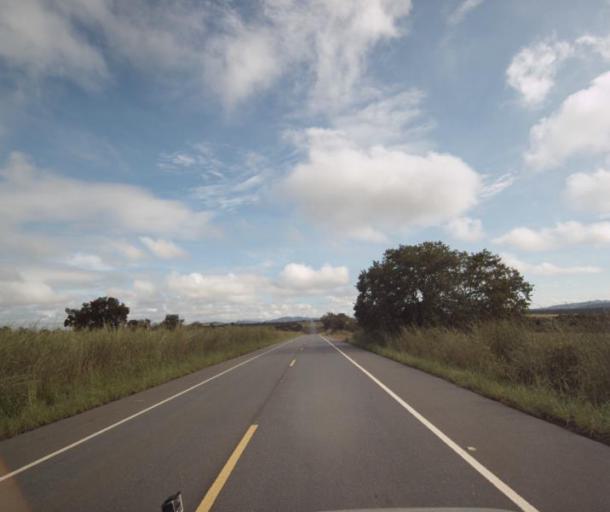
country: BR
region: Goias
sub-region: Barro Alto
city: Barro Alto
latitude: -15.2388
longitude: -48.6918
